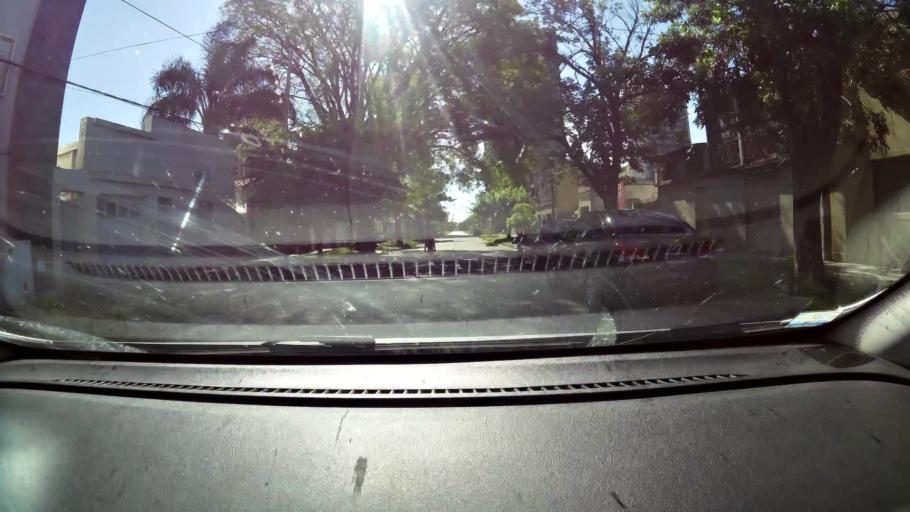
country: AR
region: Santa Fe
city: Santa Fe de la Vera Cruz
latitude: -31.6242
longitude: -60.6930
